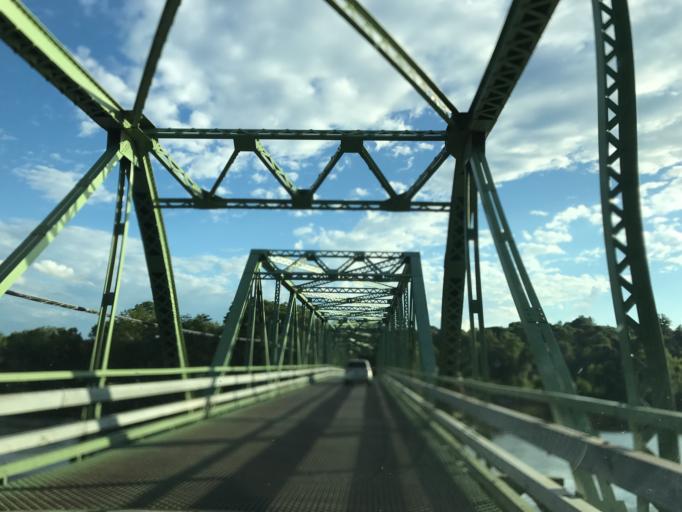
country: US
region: New York
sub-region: Saratoga County
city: Schuylerville
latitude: 43.1292
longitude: -73.5865
